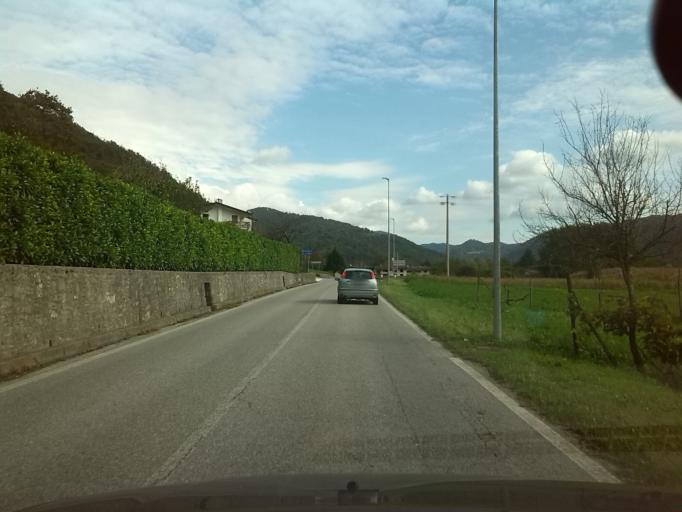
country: IT
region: Friuli Venezia Giulia
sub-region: Provincia di Udine
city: Merso di Sopra
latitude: 46.1173
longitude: 13.5103
